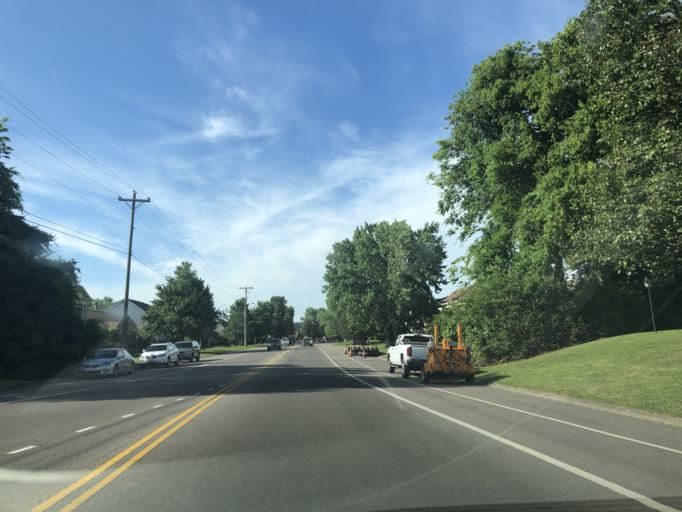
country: US
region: Tennessee
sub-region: Davidson County
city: Belle Meade
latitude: 36.0658
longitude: -86.9497
